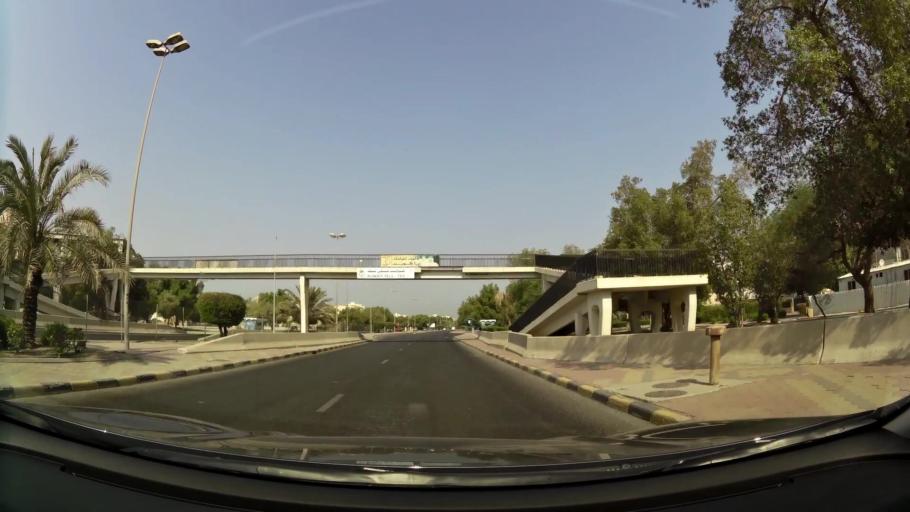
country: KW
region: Al Asimah
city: Ad Dasmah
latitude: 29.3520
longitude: 48.0149
